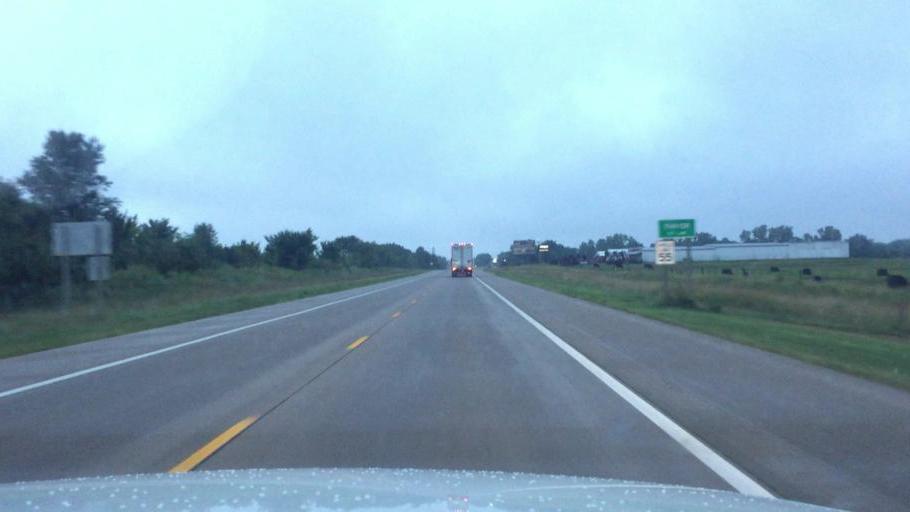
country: US
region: Kansas
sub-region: Neosho County
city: Chanute
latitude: 37.5002
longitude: -95.4706
